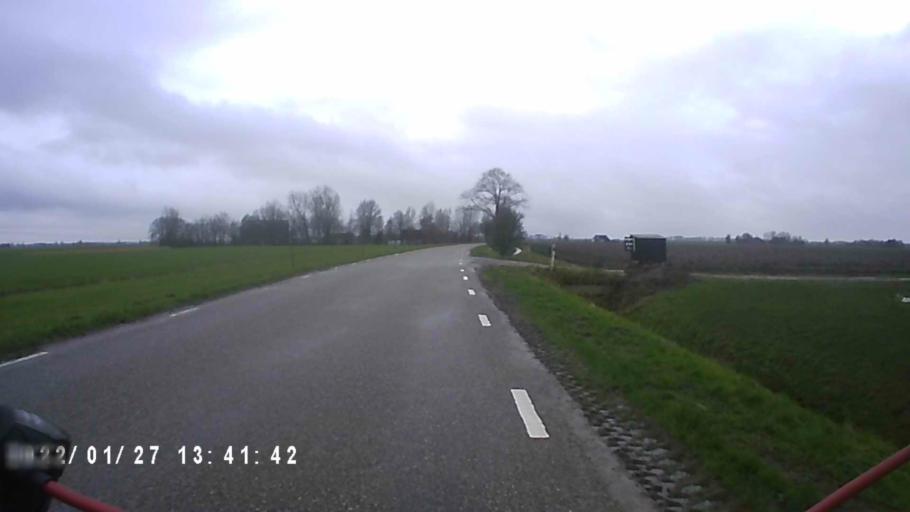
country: NL
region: Friesland
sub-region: Gemeente Kollumerland en Nieuwkruisland
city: Kollum
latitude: 53.3013
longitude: 6.2135
